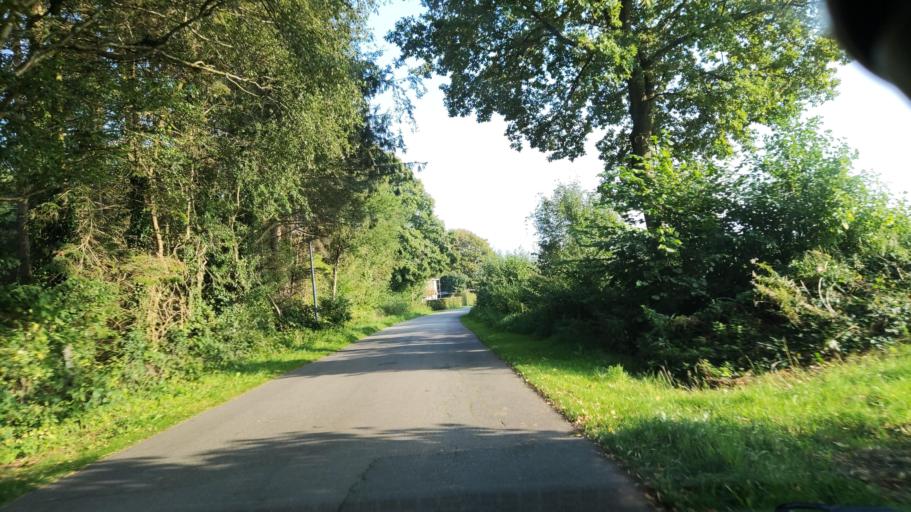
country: DE
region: Schleswig-Holstein
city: Struvenhutten
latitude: 53.8613
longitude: 10.0691
